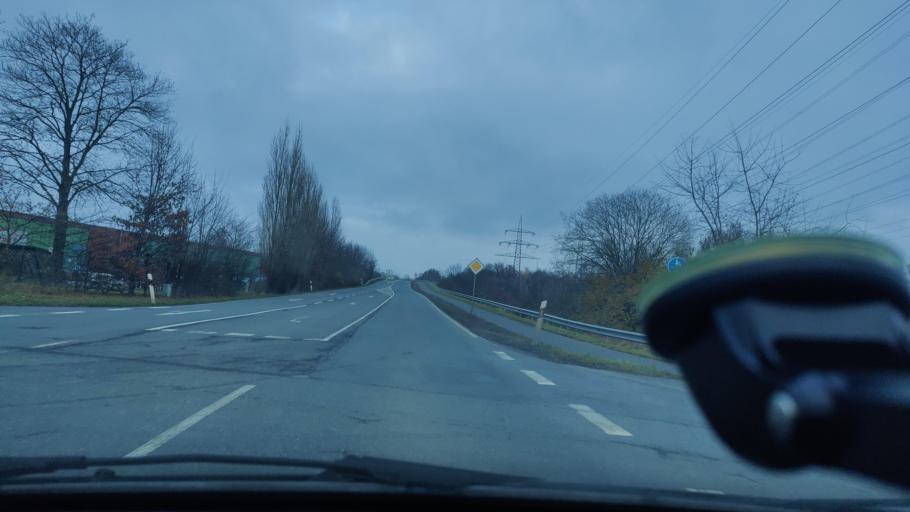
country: DE
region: North Rhine-Westphalia
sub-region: Regierungsbezirk Dusseldorf
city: Voerde
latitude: 51.6321
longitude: 6.6863
